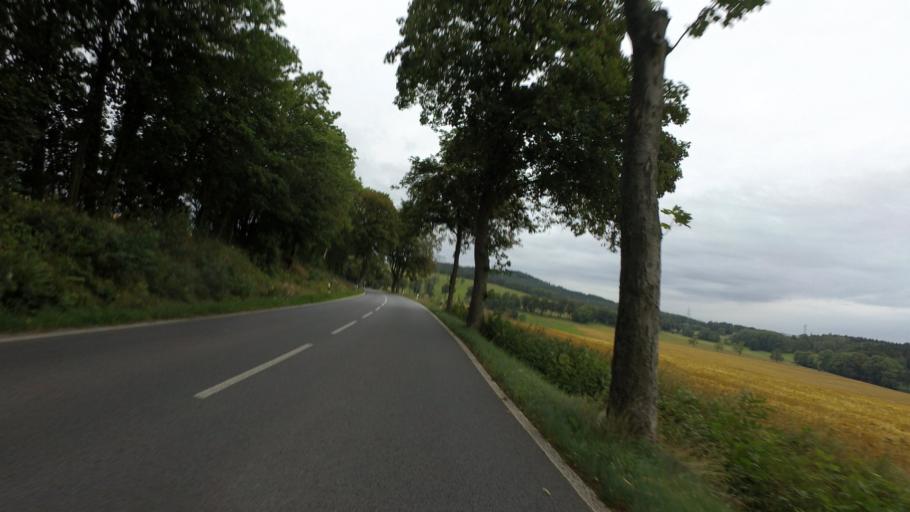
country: DE
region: Saxony
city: Berthelsdorf
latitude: 51.0781
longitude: 14.2067
